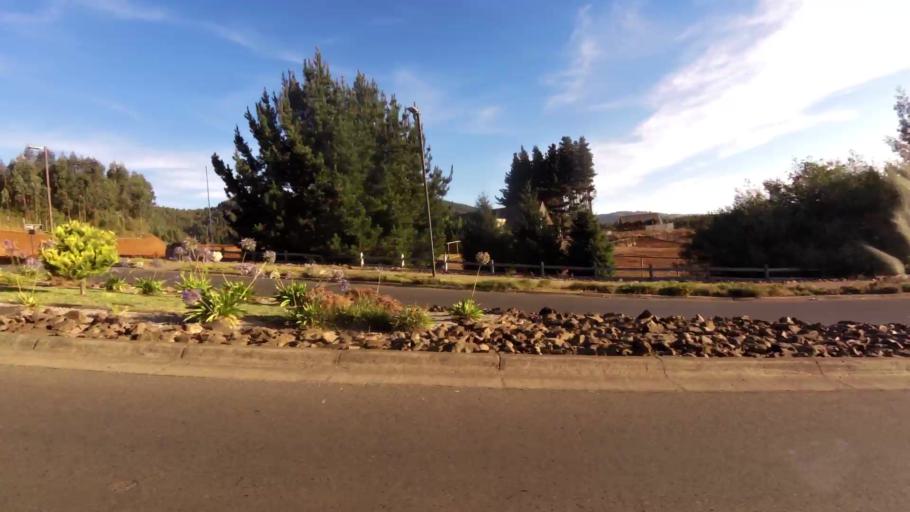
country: CL
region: Biobio
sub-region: Provincia de Concepcion
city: Concepcion
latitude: -36.8631
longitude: -73.0964
